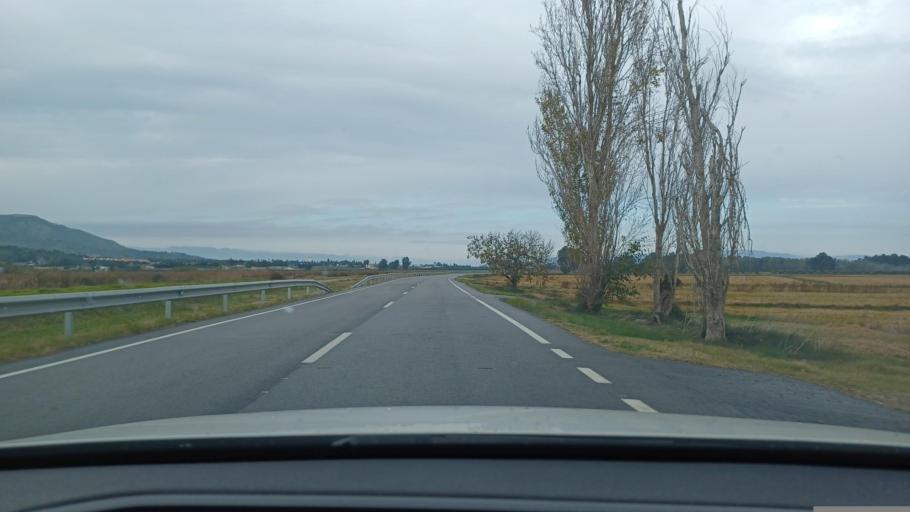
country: ES
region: Catalonia
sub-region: Provincia de Tarragona
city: Sant Carles de la Rapita
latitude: 40.6609
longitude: 0.5919
